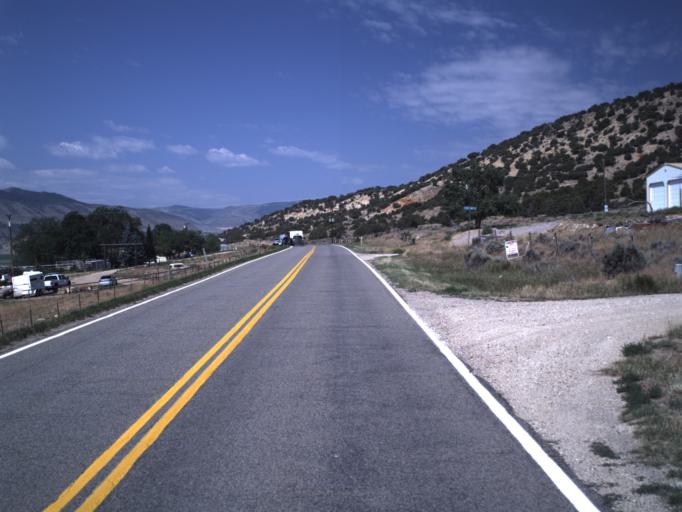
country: US
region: Utah
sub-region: Daggett County
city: Manila
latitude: 40.9772
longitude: -109.7541
